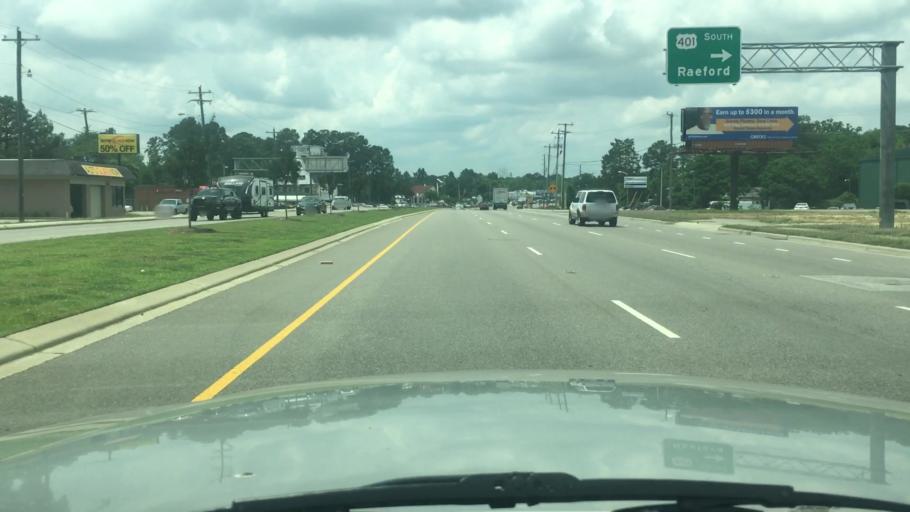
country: US
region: North Carolina
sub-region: Cumberland County
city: Fort Bragg
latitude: 35.0866
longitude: -78.9508
